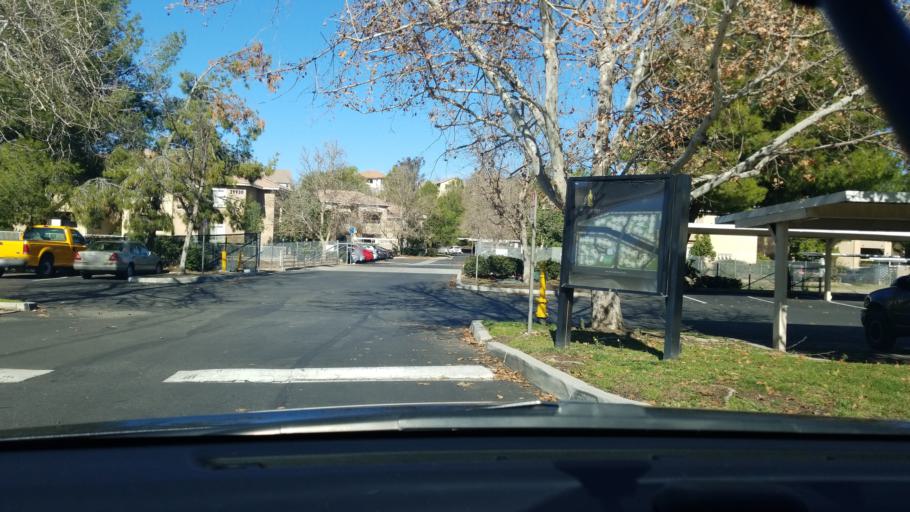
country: US
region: California
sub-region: Riverside County
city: Temecula
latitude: 33.5092
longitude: -117.1352
